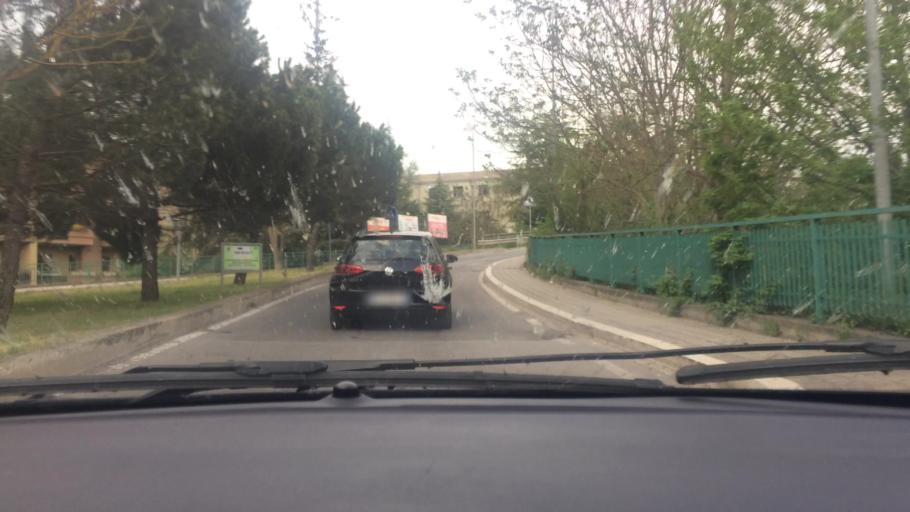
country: IT
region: Basilicate
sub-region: Provincia di Potenza
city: Potenza
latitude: 40.6508
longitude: 15.7984
